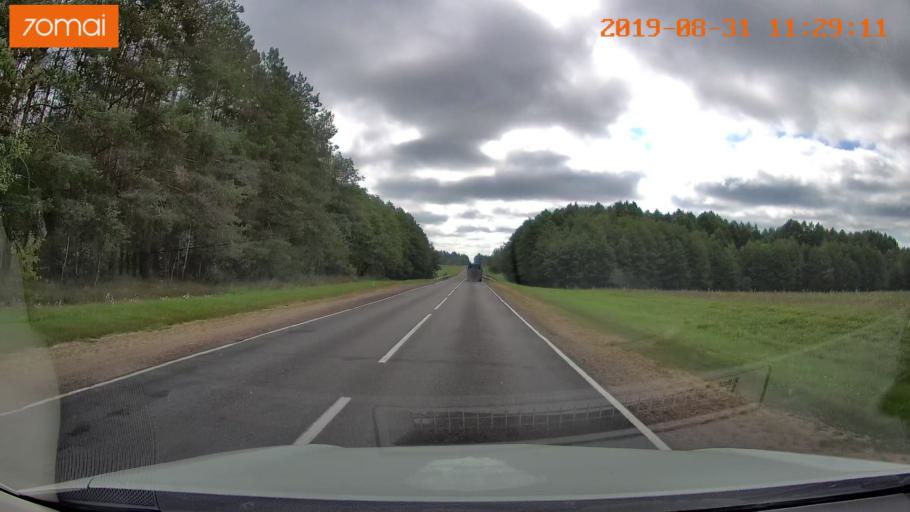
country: BY
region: Mogilev
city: Chavusy
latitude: 53.7318
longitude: 31.1163
